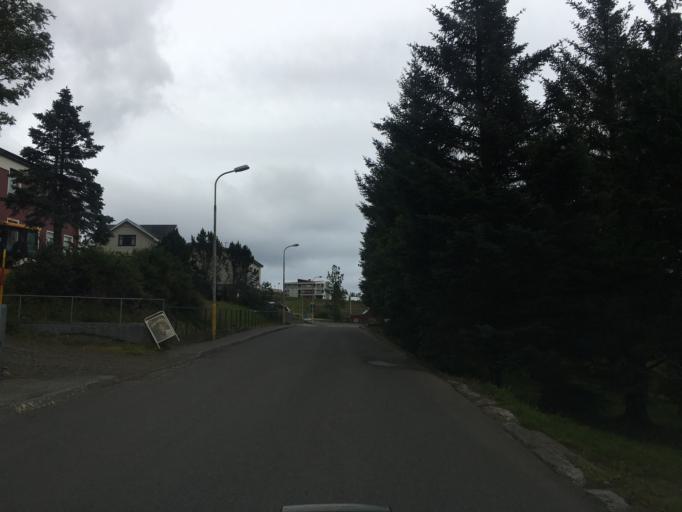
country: IS
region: East
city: Neskaupstadur
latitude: 65.1484
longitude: -13.6868
